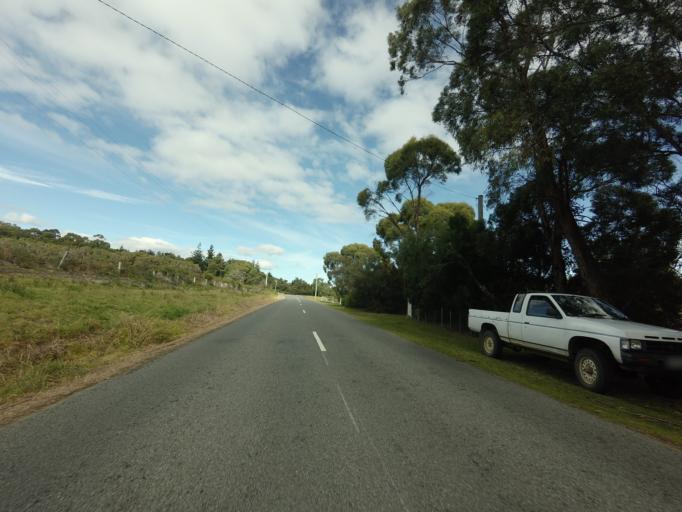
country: AU
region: Tasmania
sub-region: Clarence
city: Sandford
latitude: -43.0854
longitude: 147.7376
